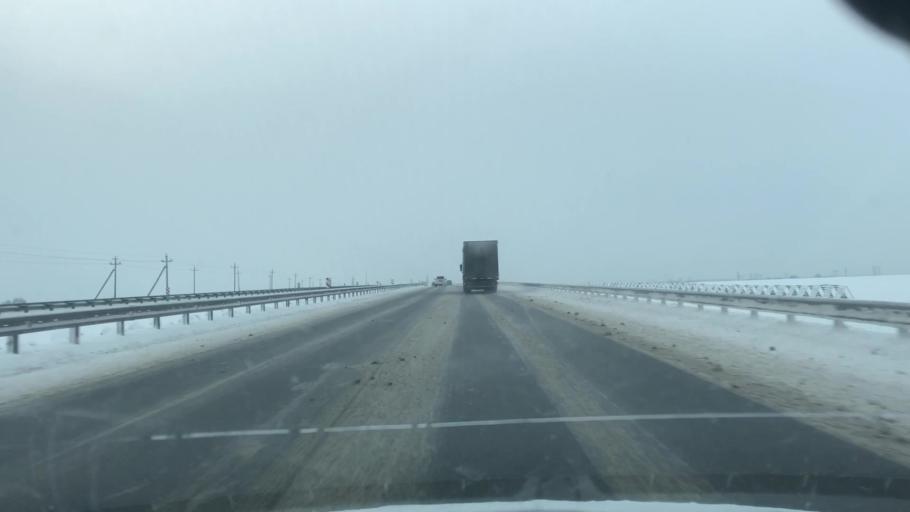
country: RU
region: Moskovskaya
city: Mikhnevo
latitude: 55.1086
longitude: 37.9261
